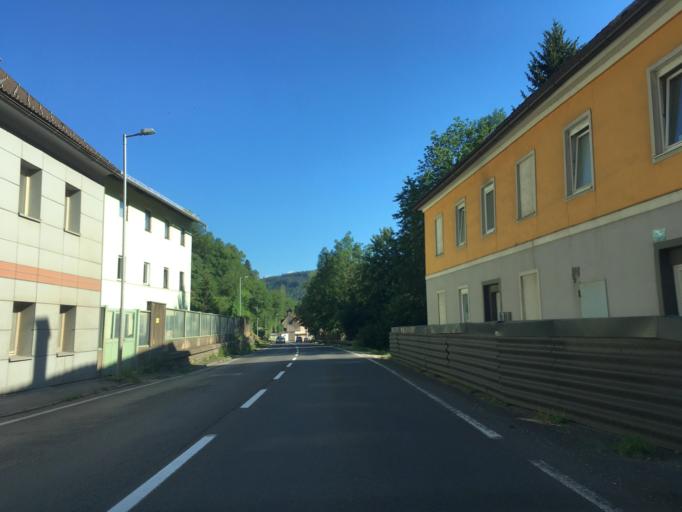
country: AT
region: Styria
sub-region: Politischer Bezirk Leoben
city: Sankt Peter-Freienstein
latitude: 47.4017
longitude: 15.0324
